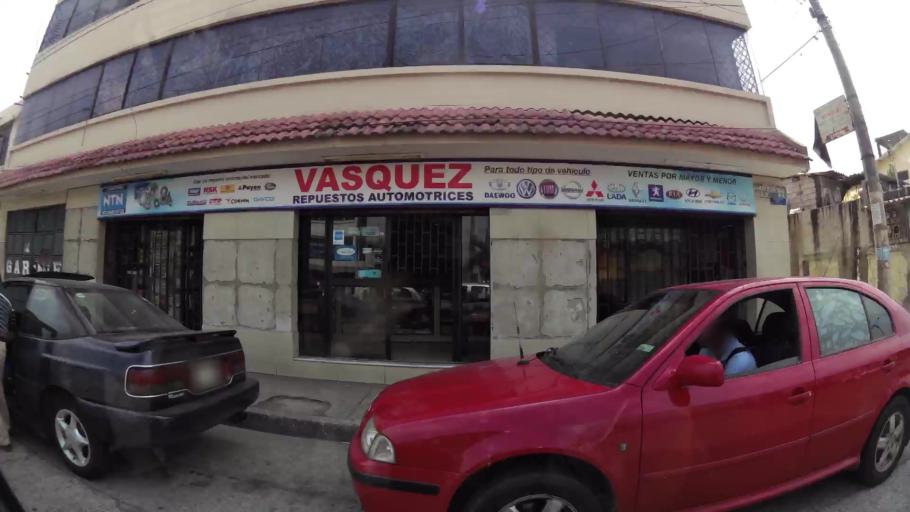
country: EC
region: Guayas
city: Eloy Alfaro
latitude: -2.1458
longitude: -79.8975
